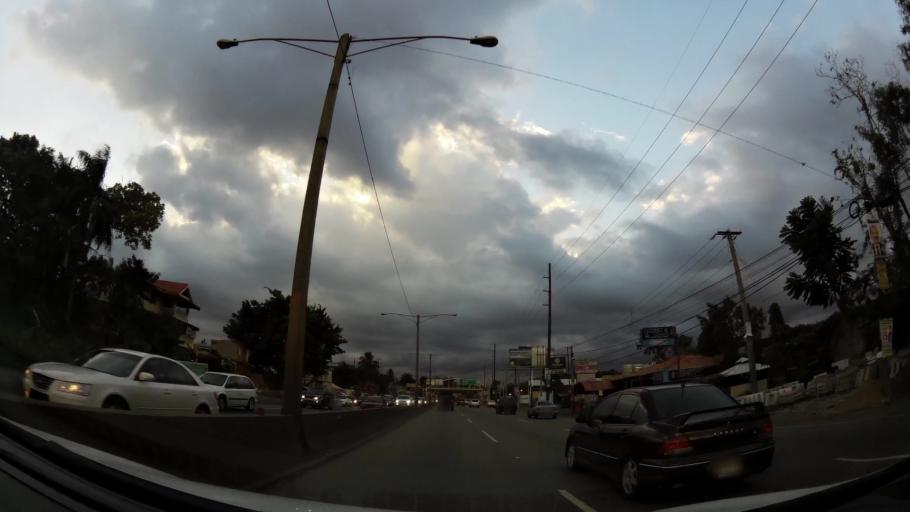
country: DO
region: Santo Domingo
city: Santo Domingo Oeste
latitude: 18.5499
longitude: -70.0502
